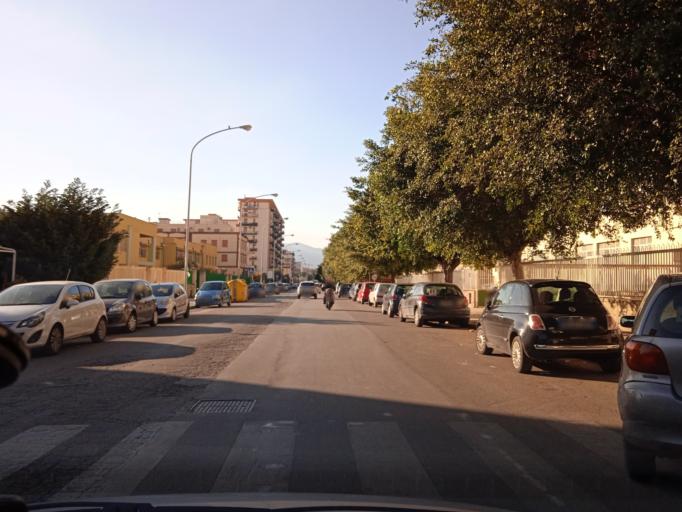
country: IT
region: Sicily
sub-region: Palermo
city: Ciaculli
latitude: 38.1037
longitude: 13.3848
